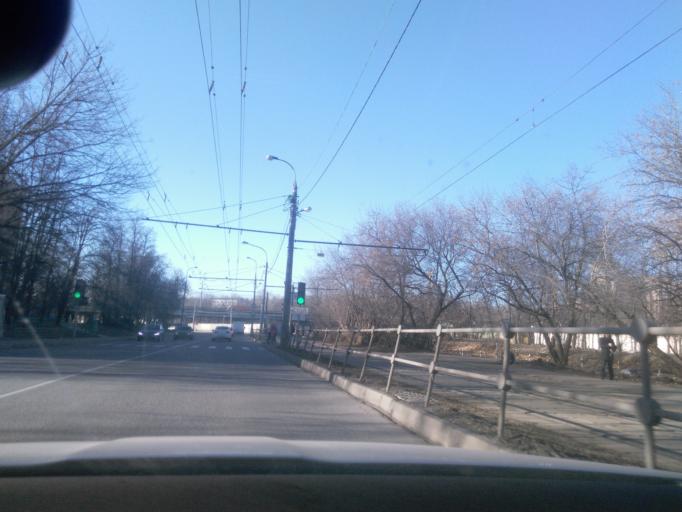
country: RU
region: Moskovskaya
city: Koptevo
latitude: 55.8117
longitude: 37.4910
